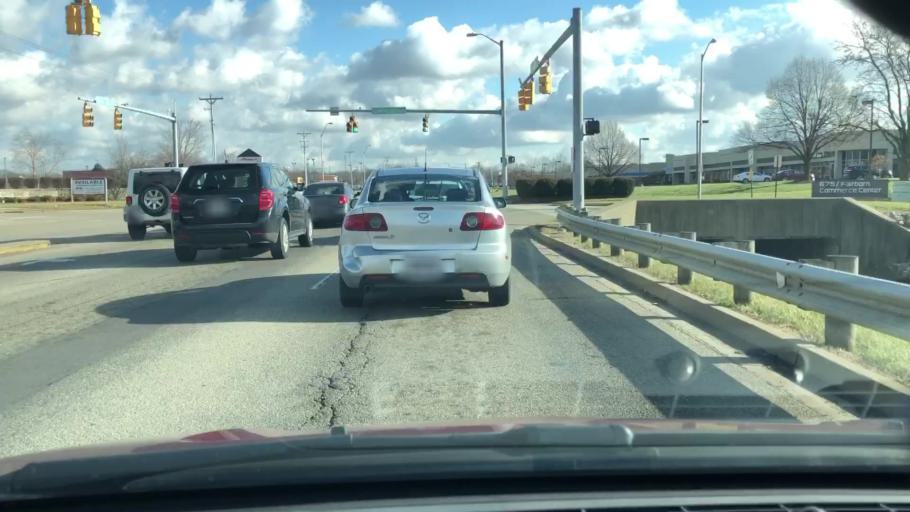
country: US
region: Ohio
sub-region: Greene County
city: Fairborn
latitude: 39.7833
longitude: -83.9979
